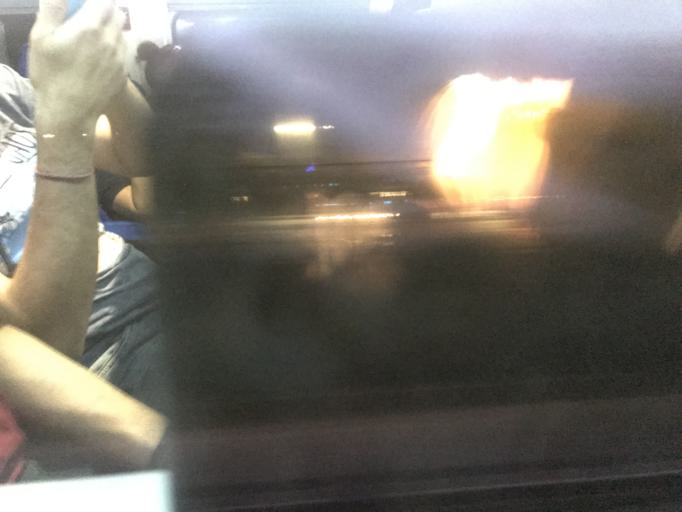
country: TR
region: Kocaeli
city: Izmit
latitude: 40.7614
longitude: 29.8989
